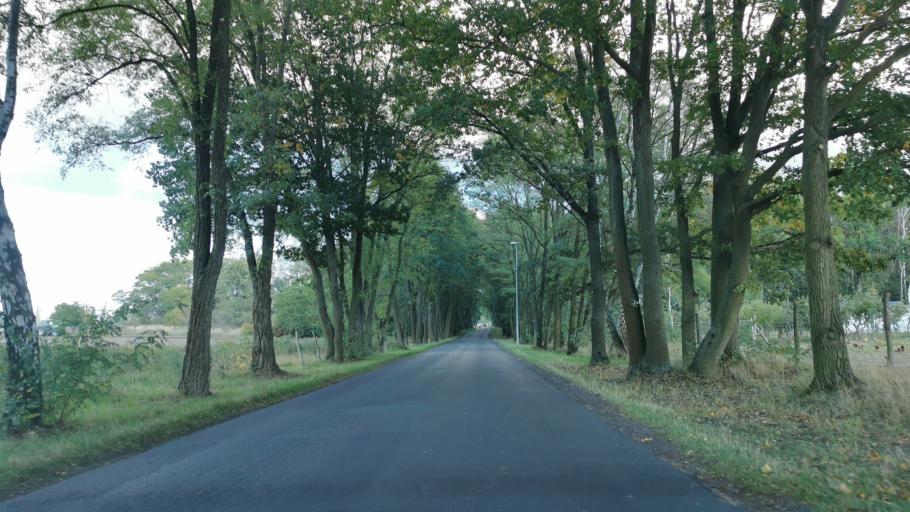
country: DE
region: Brandenburg
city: Fichtenwalde
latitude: 52.3403
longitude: 12.8863
